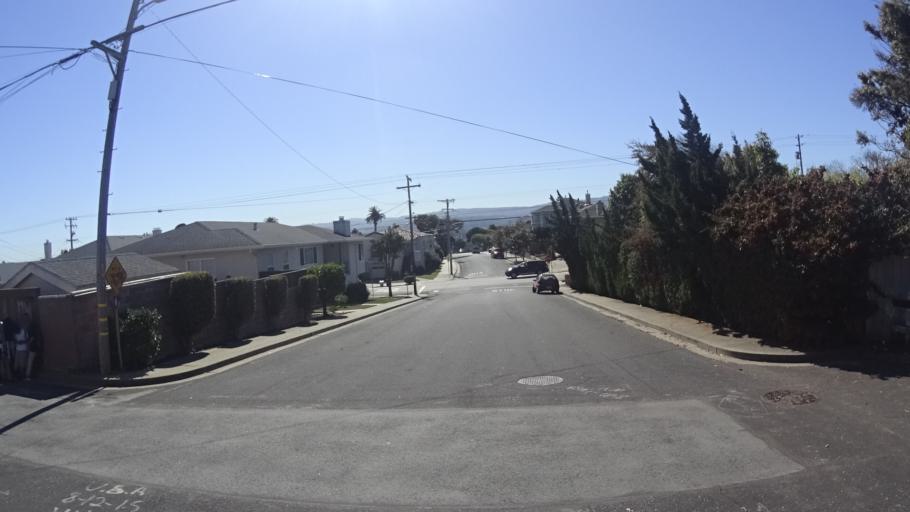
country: US
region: California
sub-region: San Mateo County
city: South San Francisco
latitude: 37.6599
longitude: -122.4244
